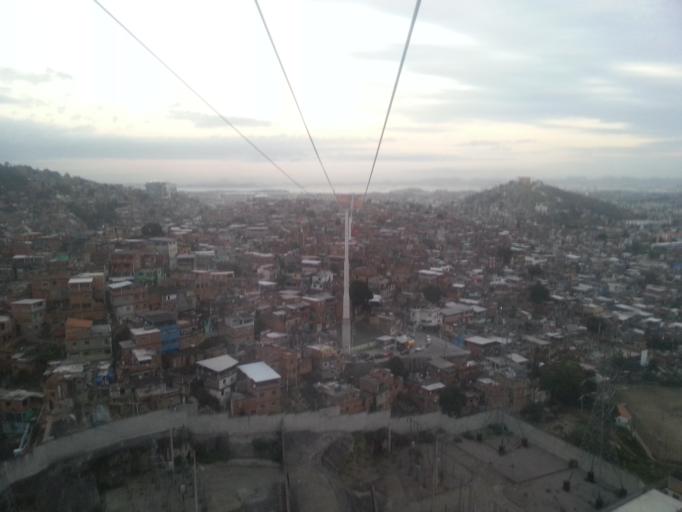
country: BR
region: Rio de Janeiro
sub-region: Rio De Janeiro
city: Rio de Janeiro
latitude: -22.8627
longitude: -43.2800
